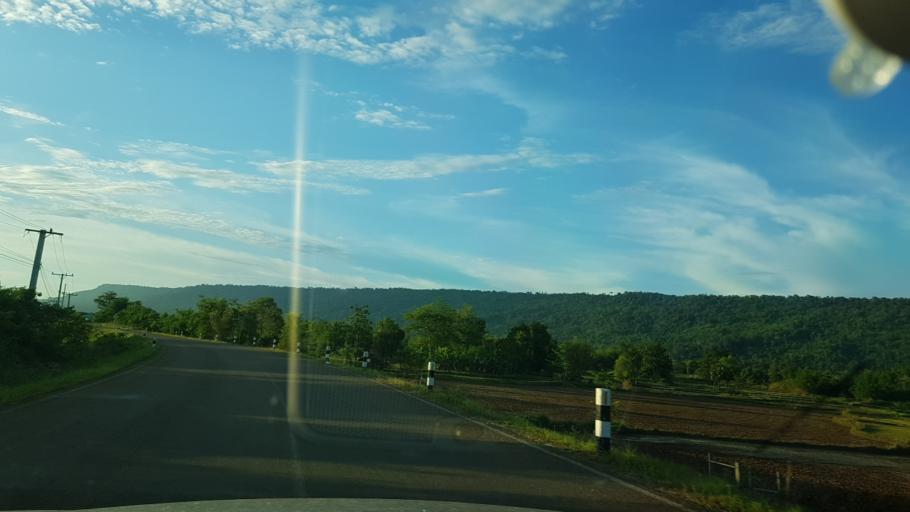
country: TH
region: Nong Khai
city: Sangkhom
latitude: 18.1084
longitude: 102.2922
